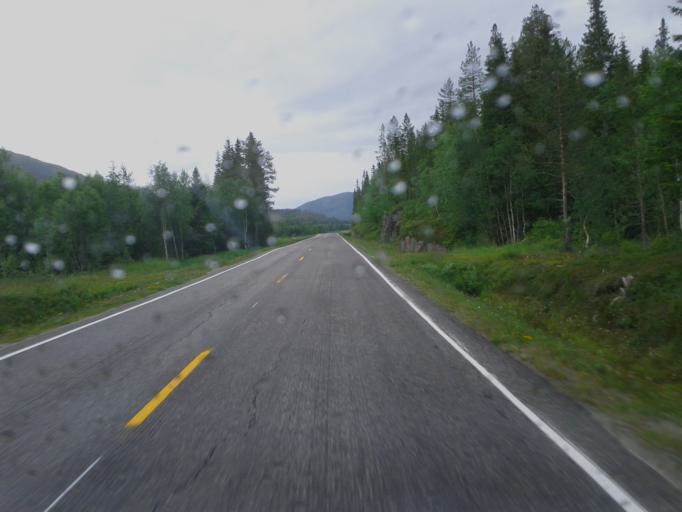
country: NO
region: Nord-Trondelag
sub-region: Namsskogan
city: Namsskogan
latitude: 64.9652
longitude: 13.2108
